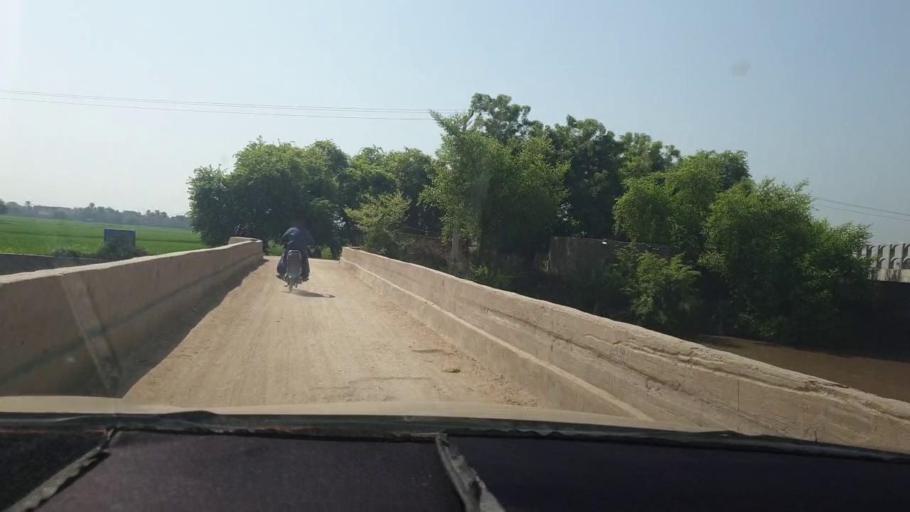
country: PK
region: Sindh
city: Kambar
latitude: 27.5767
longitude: 68.0436
